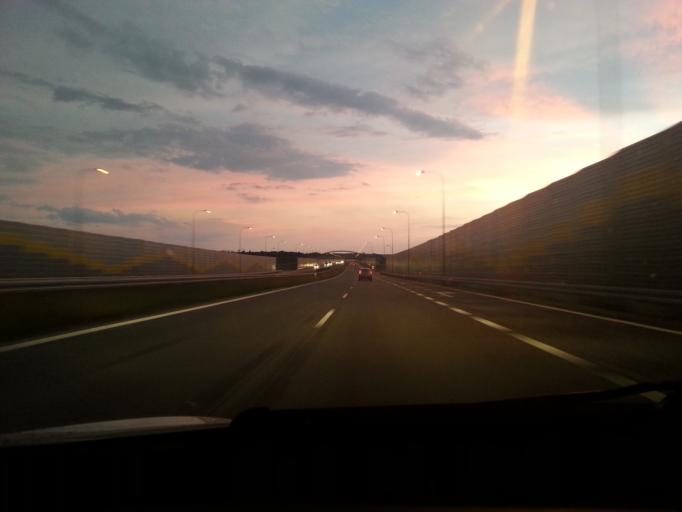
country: PL
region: Lodz Voivodeship
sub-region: Powiat zdunskowolski
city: Zdunska Wola
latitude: 51.5749
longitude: 18.9435
